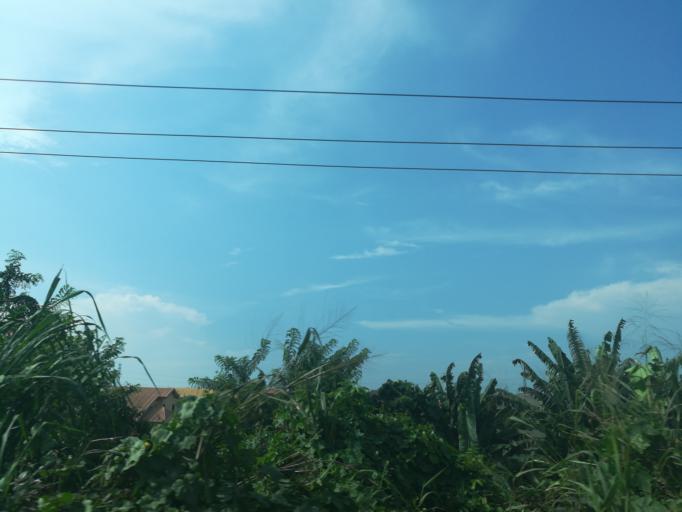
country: NG
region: Lagos
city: Ikorodu
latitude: 6.6303
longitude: 3.5168
